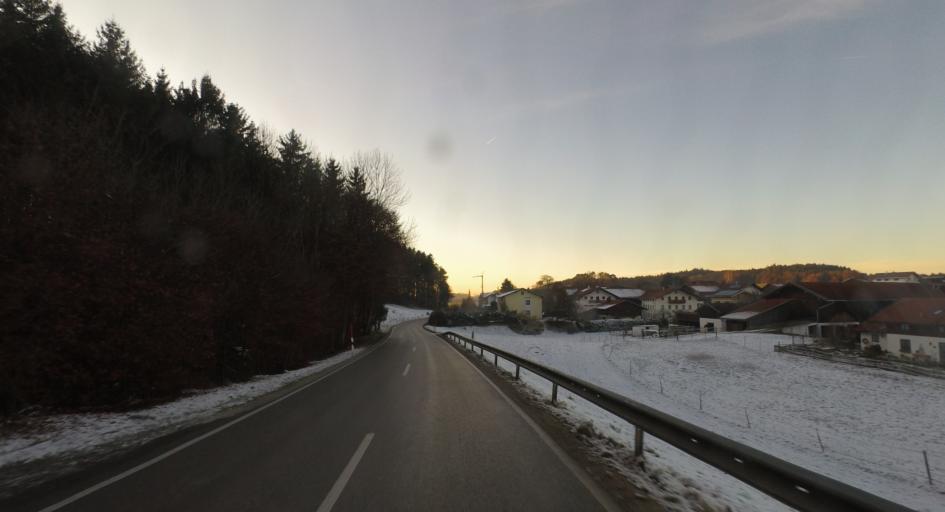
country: DE
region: Bavaria
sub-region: Upper Bavaria
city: Nussdorf
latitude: 47.8866
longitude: 12.5948
